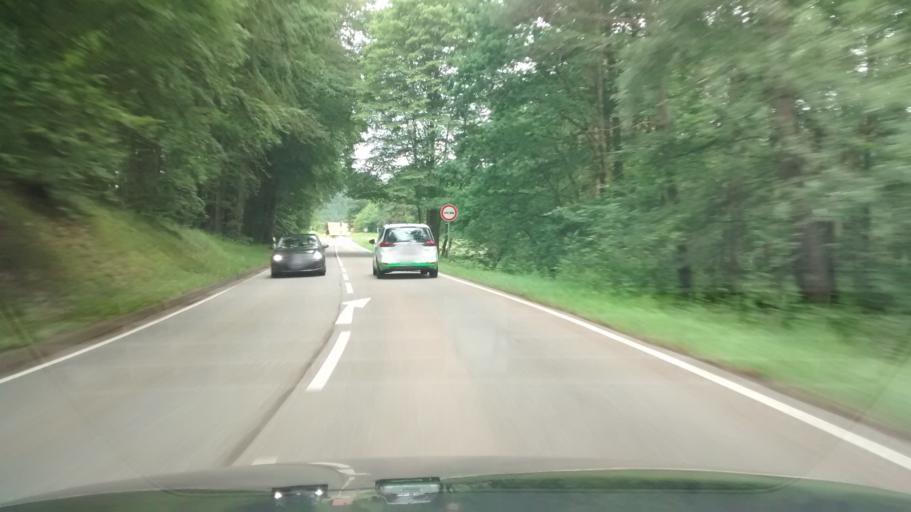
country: DE
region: Rheinland-Pfalz
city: Birkenhordt
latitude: 49.1146
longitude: 7.9100
